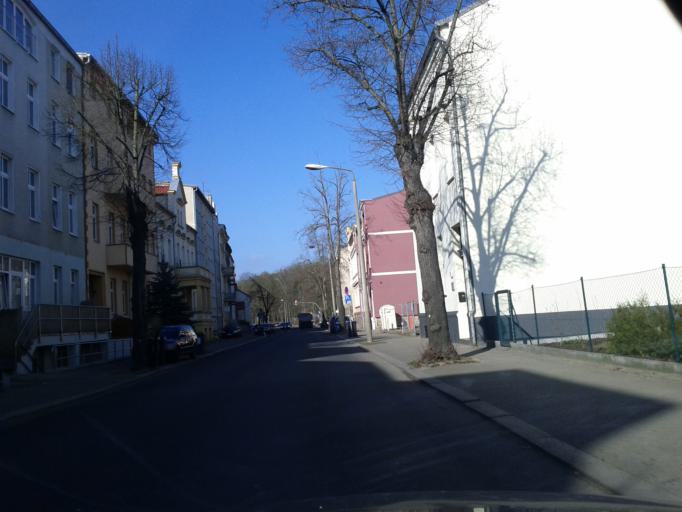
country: DE
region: Brandenburg
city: Furstenwalde
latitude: 52.3624
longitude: 14.0587
